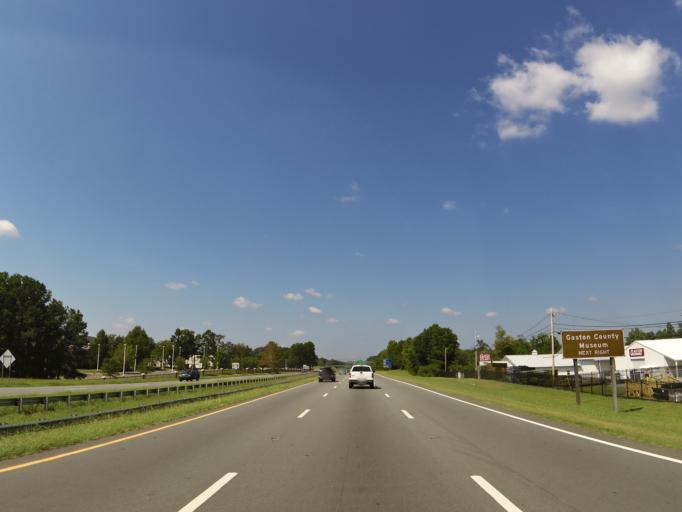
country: US
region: North Carolina
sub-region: Gaston County
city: Dallas
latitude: 35.3083
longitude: -81.1874
